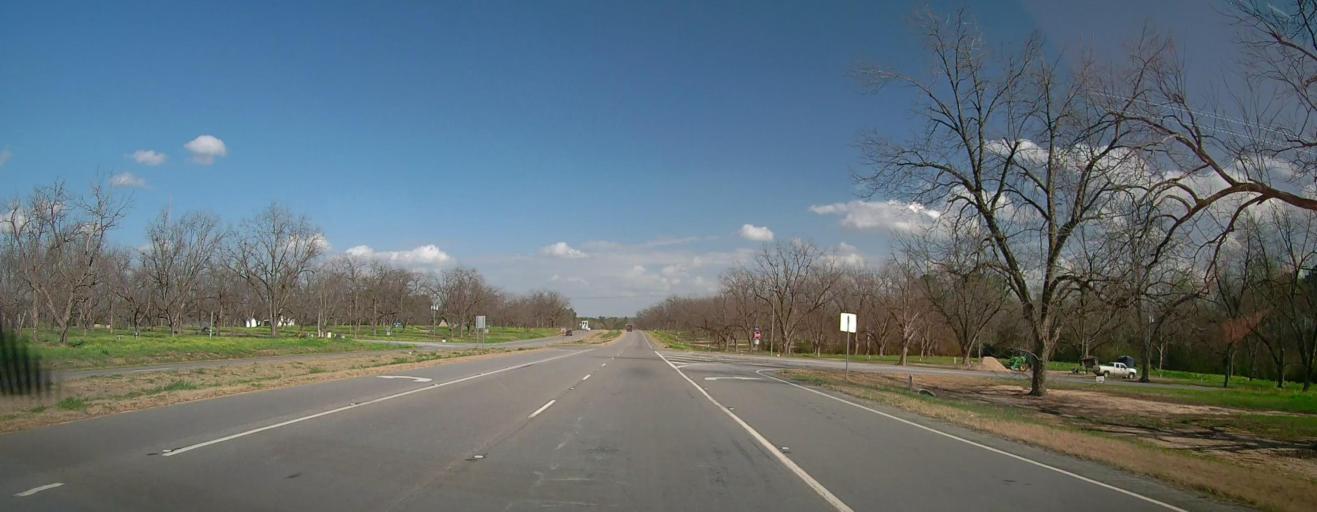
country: US
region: Georgia
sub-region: Dodge County
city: Eastman
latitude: 32.1986
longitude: -83.2285
